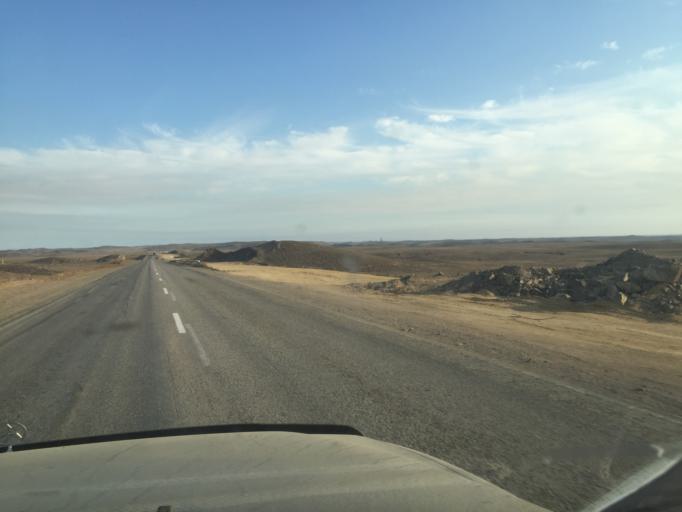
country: KZ
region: Zhambyl
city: Mynaral
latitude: 45.4620
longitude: 73.5773
